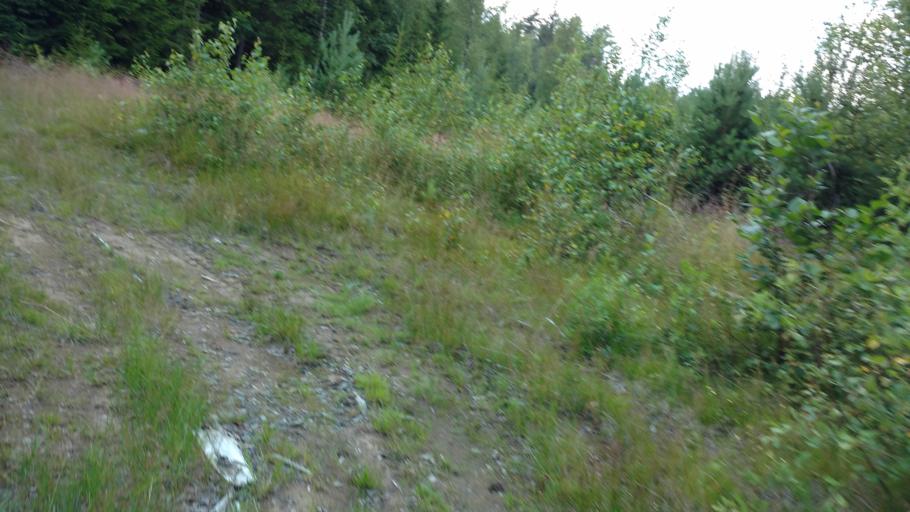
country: FI
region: Varsinais-Suomi
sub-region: Salo
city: Pertteli
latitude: 60.3963
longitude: 23.2251
